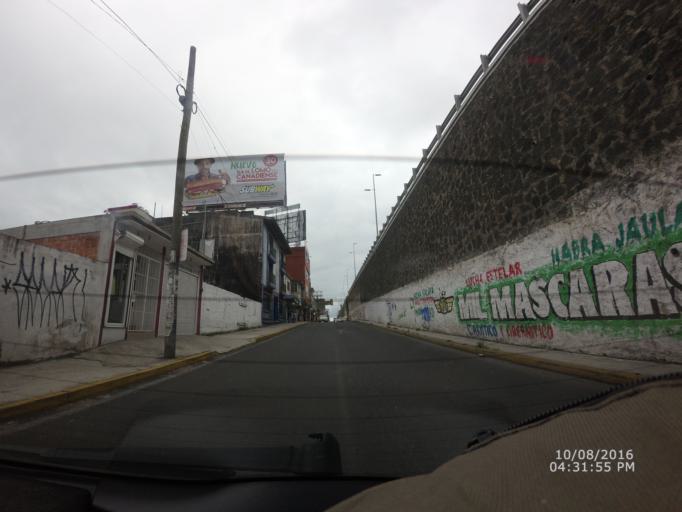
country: MX
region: Veracruz
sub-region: Xalapa
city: Xalapa de Enriquez
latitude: 19.5519
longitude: -96.9131
